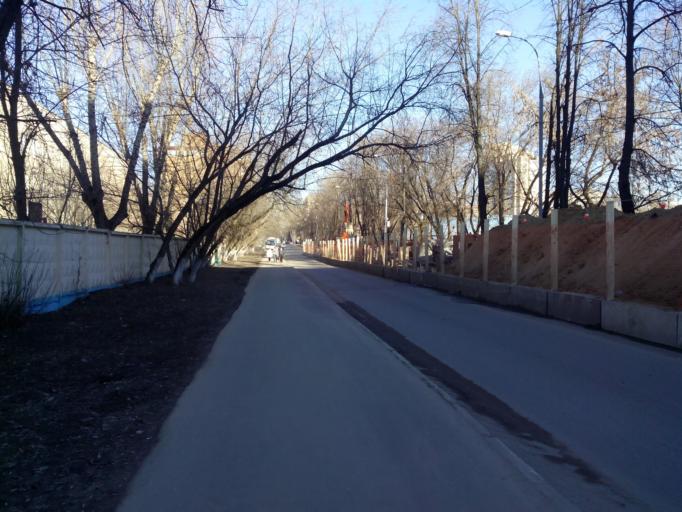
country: RU
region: Moscow
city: Lefortovo
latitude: 55.7763
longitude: 37.7269
